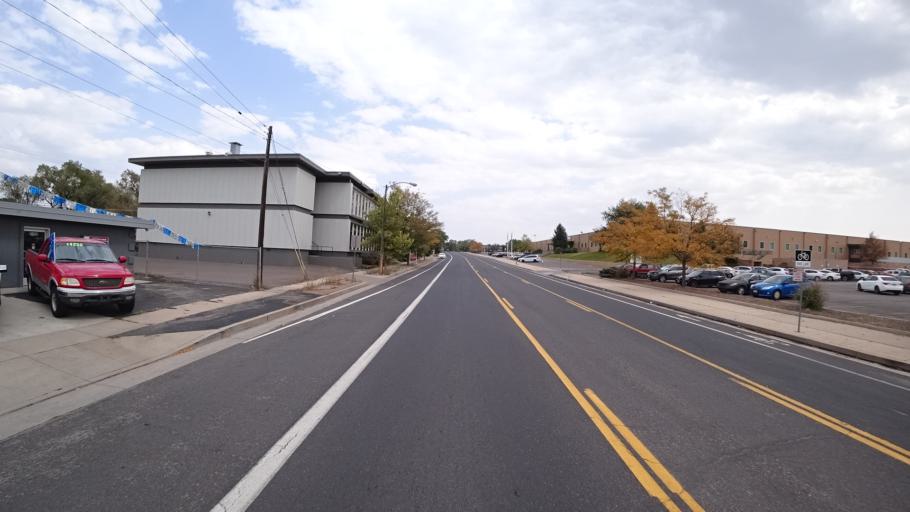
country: US
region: Colorado
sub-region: El Paso County
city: Colorado Springs
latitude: 38.8356
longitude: -104.7896
